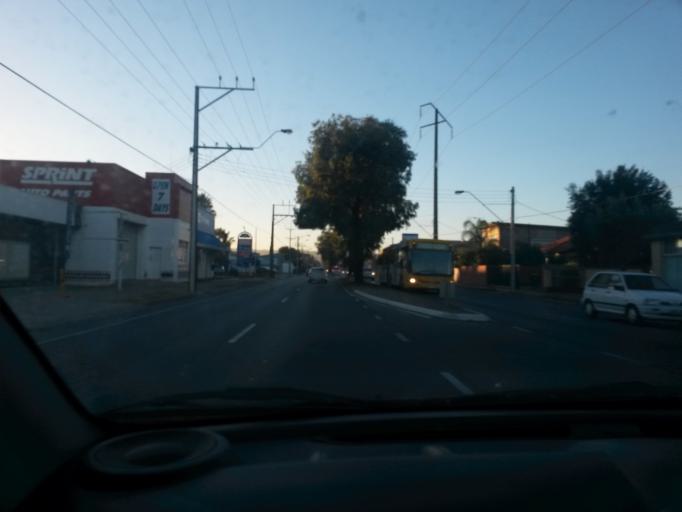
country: AU
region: South Australia
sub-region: Charles Sturt
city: Woodville
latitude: -34.8787
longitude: 138.5543
